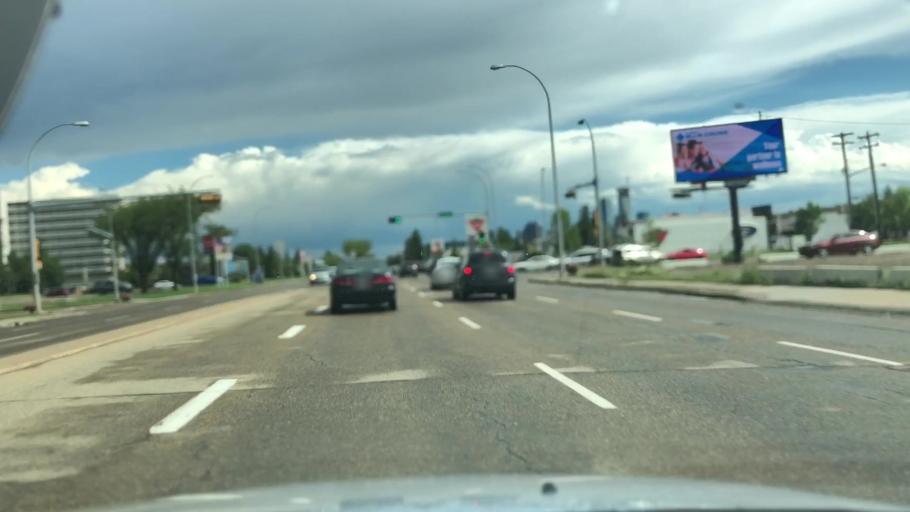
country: CA
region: Alberta
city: Edmonton
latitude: 53.5688
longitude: -113.5273
